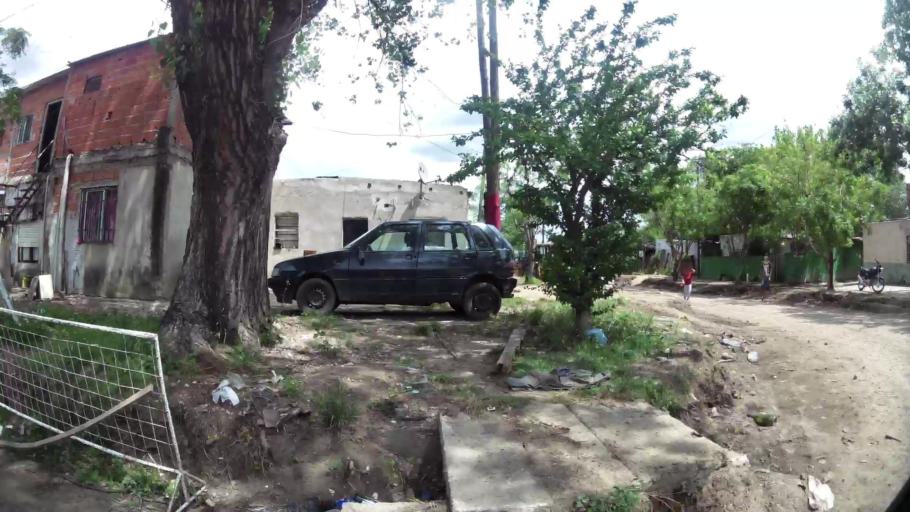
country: AR
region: Santa Fe
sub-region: Departamento de Rosario
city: Rosario
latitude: -32.9804
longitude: -60.6596
